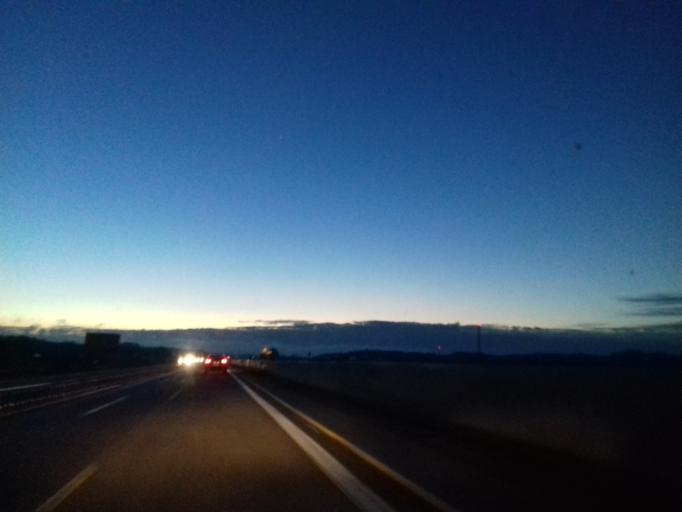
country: CZ
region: Vysocina
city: Merin
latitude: 49.3812
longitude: 15.9383
